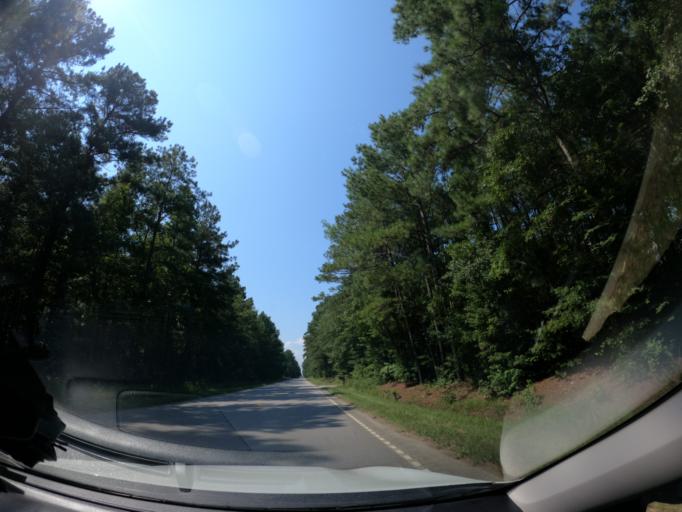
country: US
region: South Carolina
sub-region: Richland County
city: Hopkins
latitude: 33.8697
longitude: -80.8936
